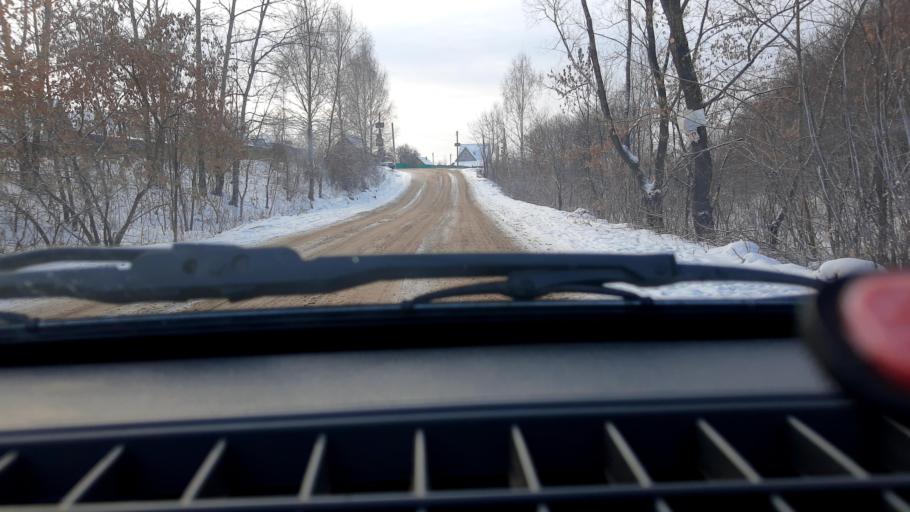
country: RU
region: Bashkortostan
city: Iglino
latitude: 54.7974
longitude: 56.3140
